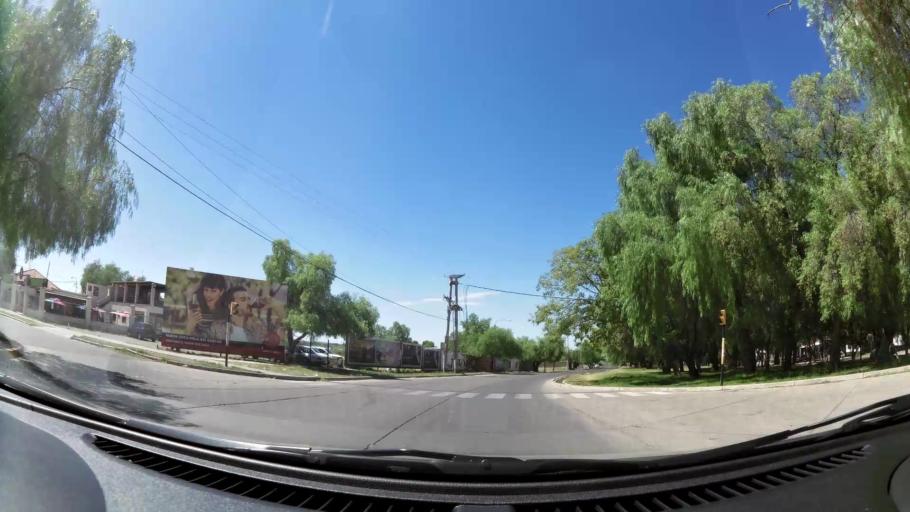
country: AR
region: Mendoza
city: Las Heras
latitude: -32.8529
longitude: -68.8582
